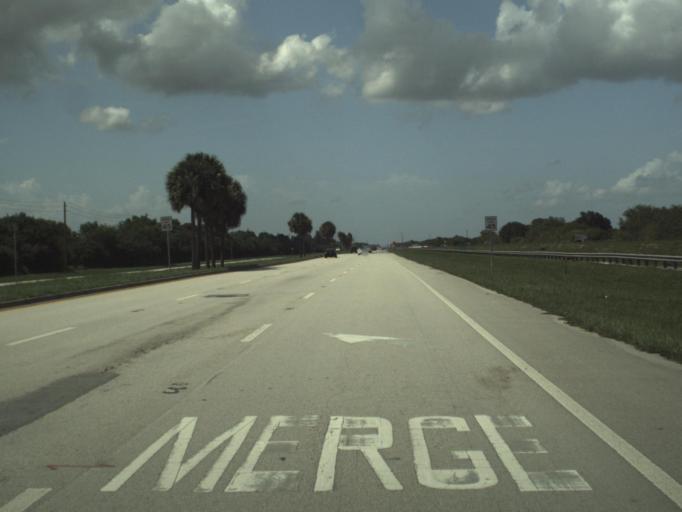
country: US
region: Florida
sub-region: Palm Beach County
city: Villages of Oriole
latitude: 26.4161
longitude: -80.2039
